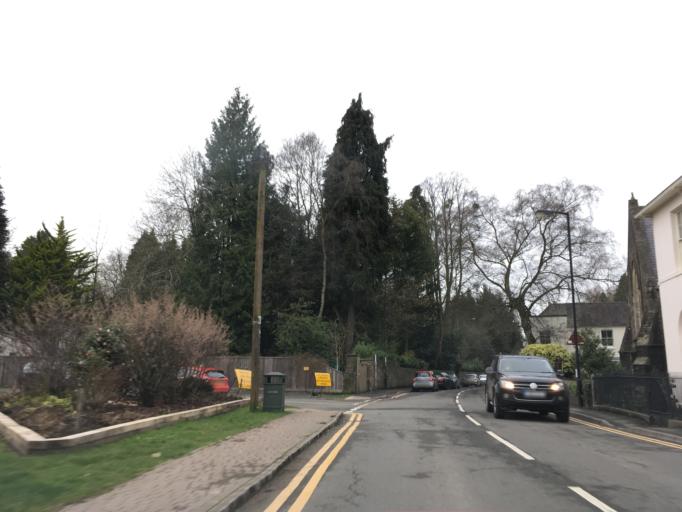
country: GB
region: Wales
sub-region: Monmouthshire
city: Usk
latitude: 51.7041
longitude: -2.9040
